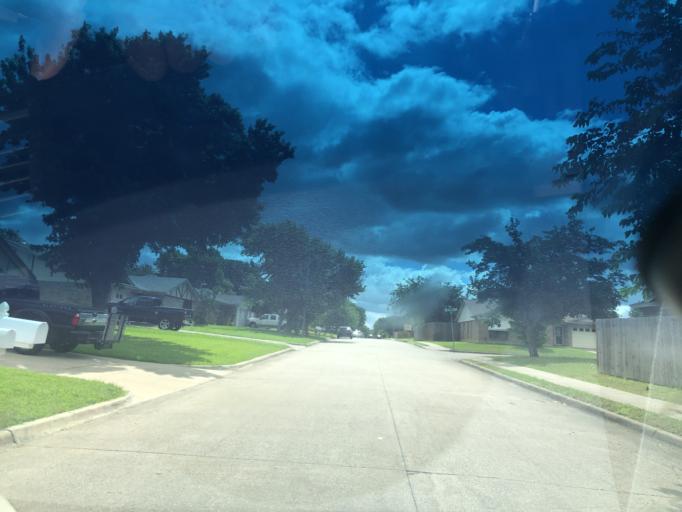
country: US
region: Texas
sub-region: Dallas County
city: Grand Prairie
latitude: 32.7071
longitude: -97.0413
